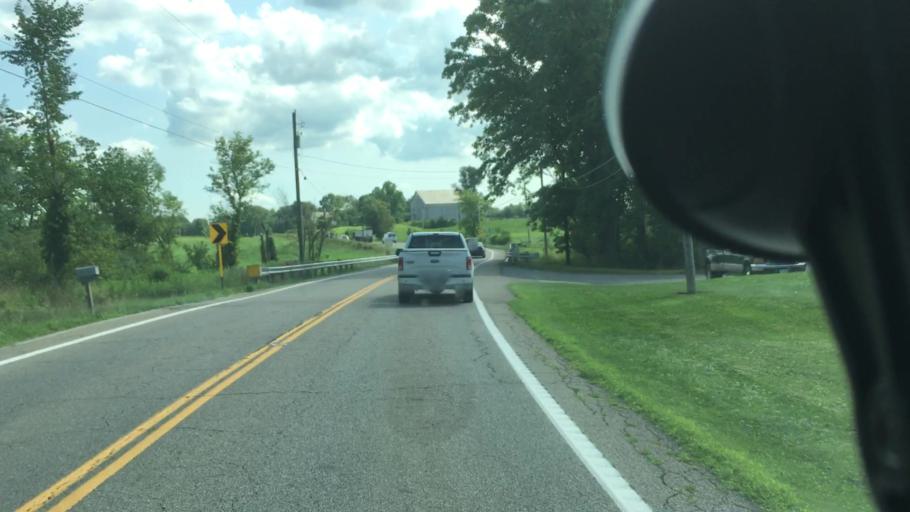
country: US
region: Ohio
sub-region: Mahoning County
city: Canfield
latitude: 40.9770
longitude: -80.8267
